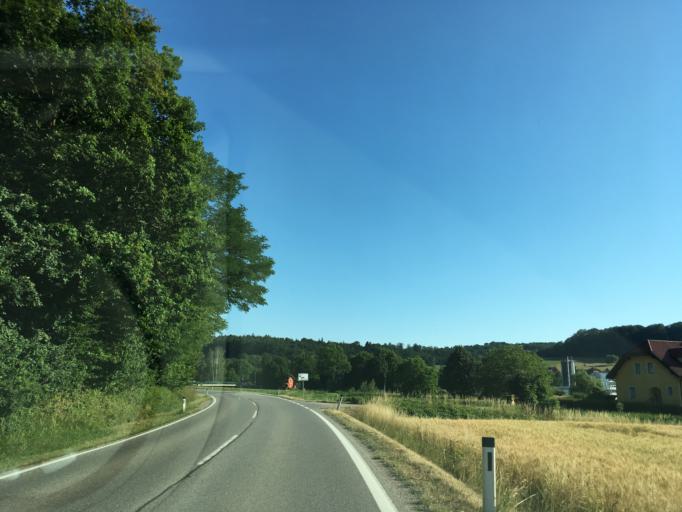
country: AT
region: Lower Austria
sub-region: Politischer Bezirk Sankt Polten
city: Boheimkirchen
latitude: 48.1709
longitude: 15.7532
